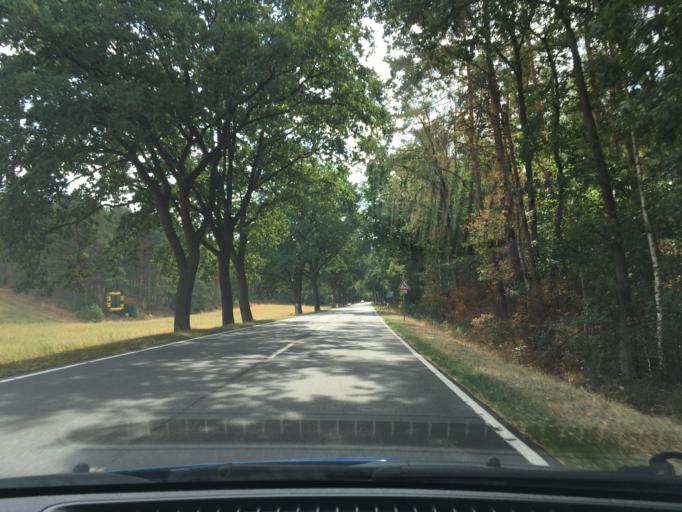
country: DE
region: Lower Saxony
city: Karwitz
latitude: 53.1270
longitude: 10.9749
